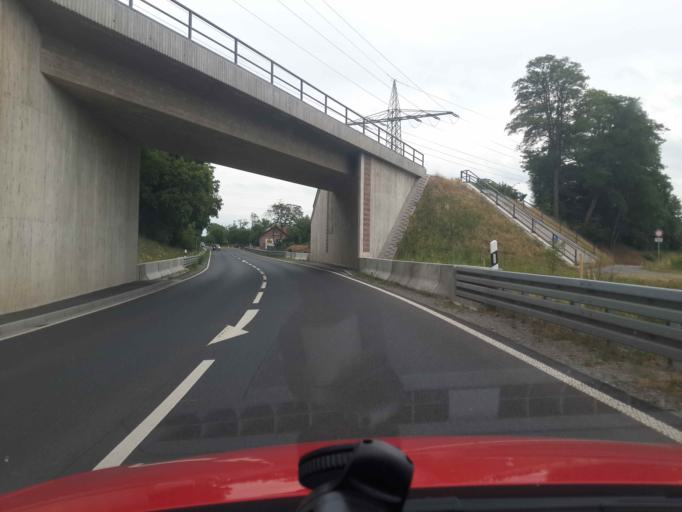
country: DE
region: Bavaria
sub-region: Regierungsbezirk Unterfranken
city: Aschaffenburg
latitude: 49.9530
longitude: 9.1279
